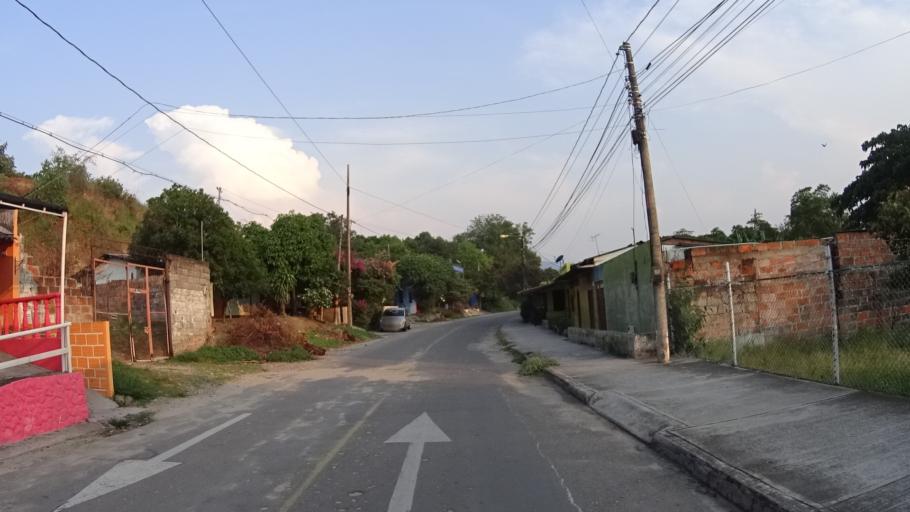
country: CO
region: Cundinamarca
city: Puerto Salgar
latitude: 5.4709
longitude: -74.6685
